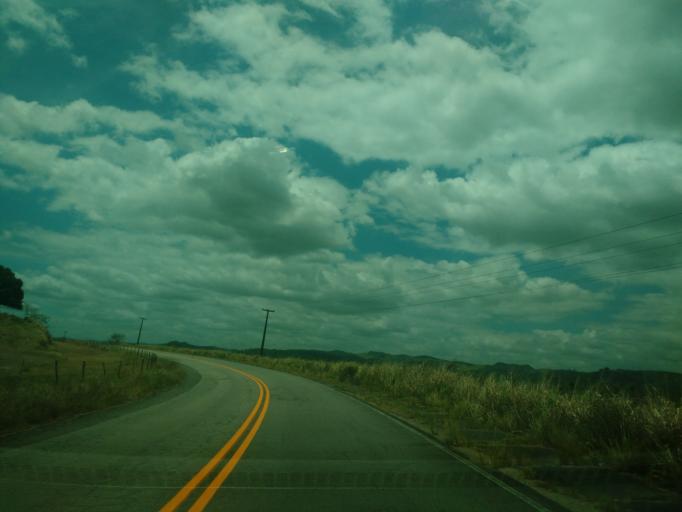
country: BR
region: Alagoas
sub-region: Uniao Dos Palmares
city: Uniao dos Palmares
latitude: -9.1435
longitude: -36.0636
